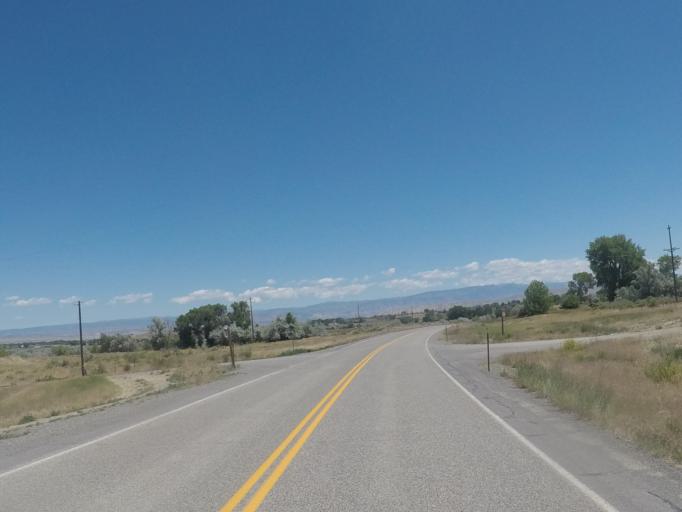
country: US
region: Wyoming
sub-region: Big Horn County
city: Lovell
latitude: 44.7961
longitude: -108.4504
